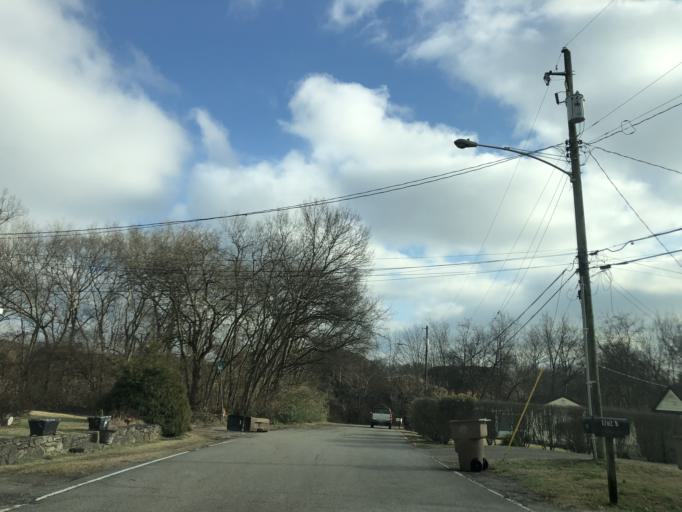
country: US
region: Tennessee
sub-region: Davidson County
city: Nashville
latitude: 36.2016
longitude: -86.7842
